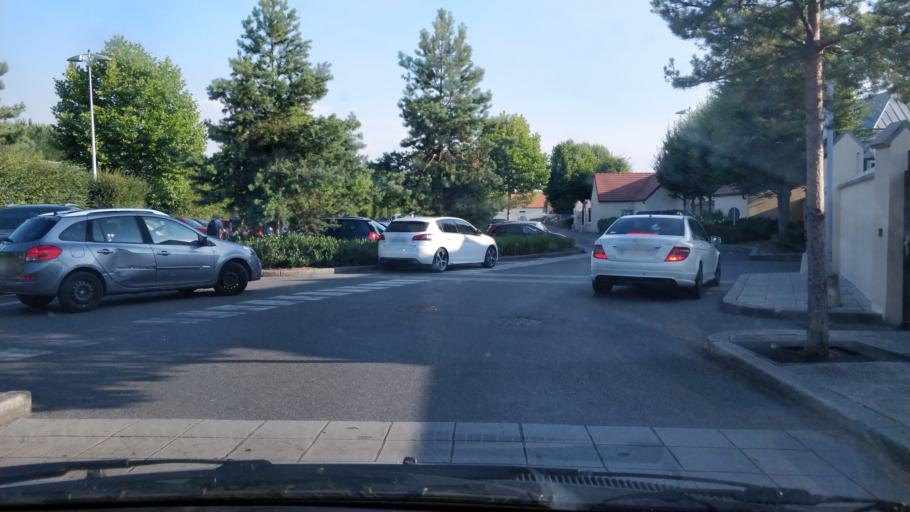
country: FR
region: Ile-de-France
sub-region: Departement de Seine-et-Marne
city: Serris
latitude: 48.8544
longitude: 2.7845
